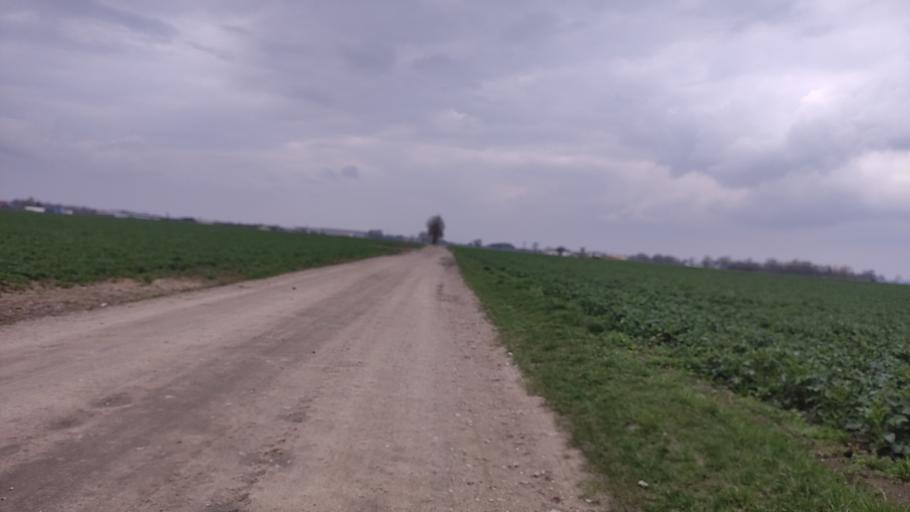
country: PL
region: Greater Poland Voivodeship
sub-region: Powiat poznanski
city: Swarzedz
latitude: 52.4031
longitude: 17.1514
